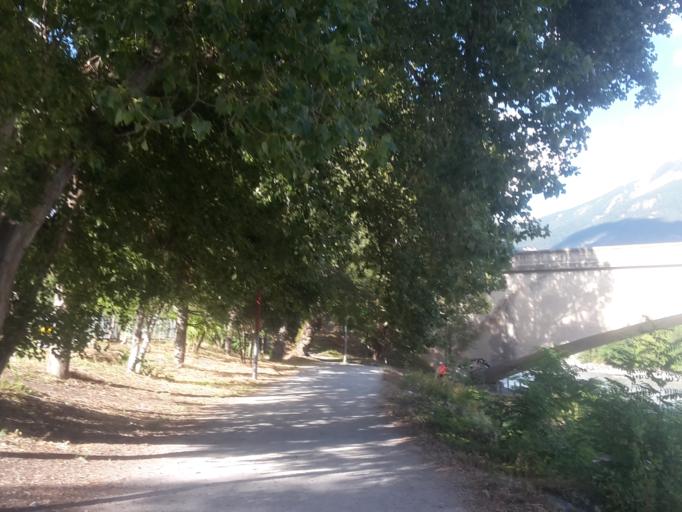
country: FR
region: Provence-Alpes-Cote d'Azur
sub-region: Departement des Hautes-Alpes
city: Embrun
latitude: 44.5503
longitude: 6.4837
